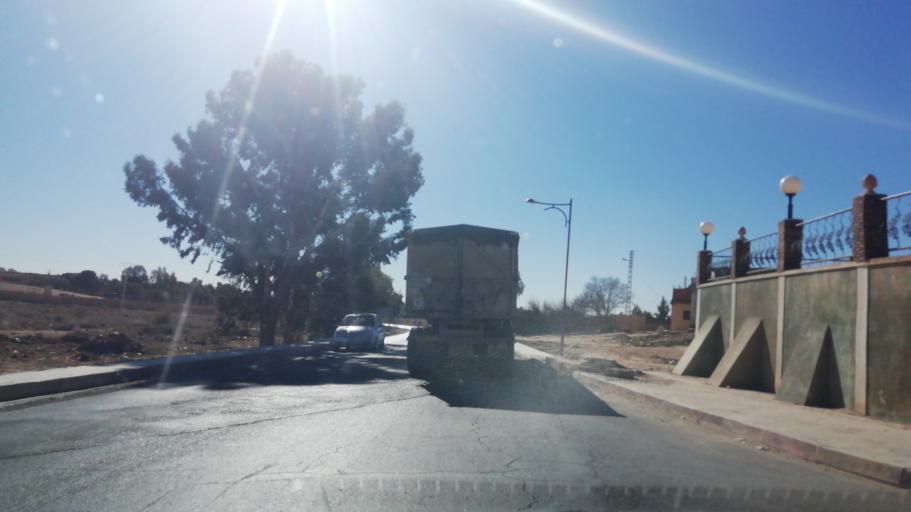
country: DZ
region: Saida
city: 'Ain el Hadjar
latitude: 34.1493
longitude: 0.0696
